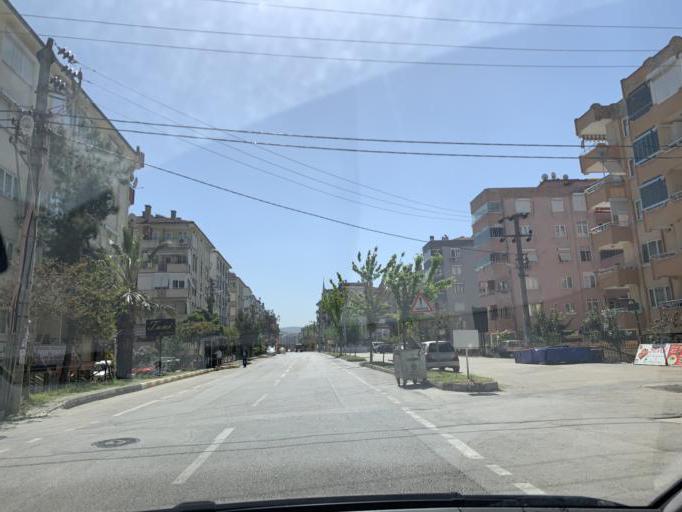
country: TR
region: Bursa
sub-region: Mudanya
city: Mudanya
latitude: 40.3598
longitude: 28.9128
